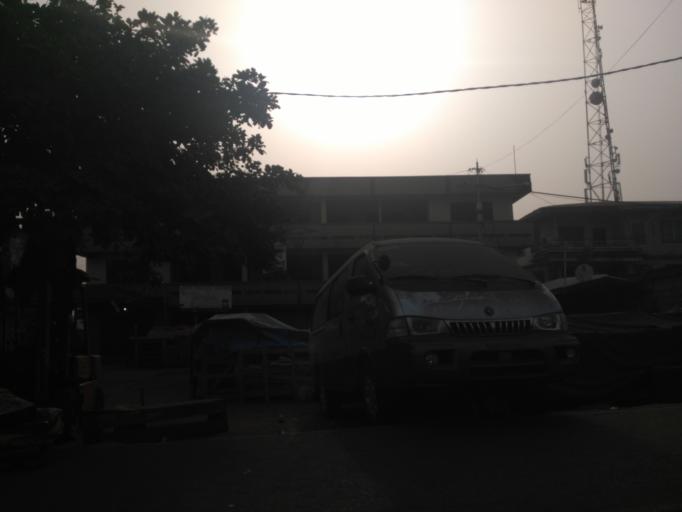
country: GH
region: Ashanti
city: Tafo
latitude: 6.7209
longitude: -1.6329
